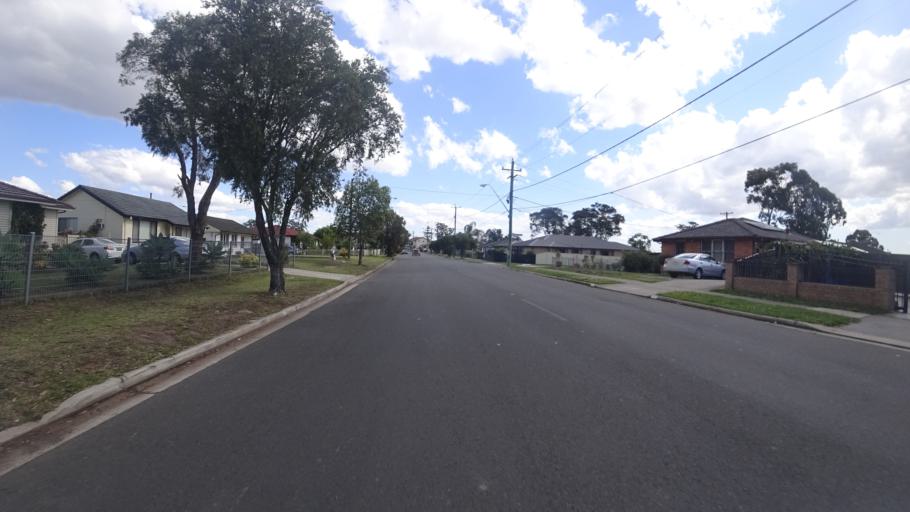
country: AU
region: New South Wales
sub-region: Fairfield
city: Cabramatta West
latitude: -33.8979
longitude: 150.9117
